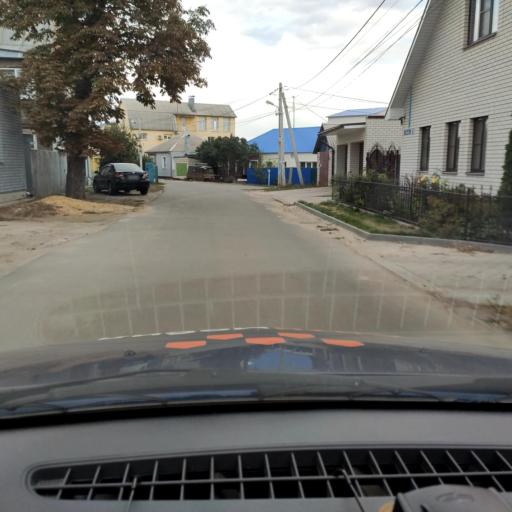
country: RU
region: Voronezj
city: Voronezh
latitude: 51.6279
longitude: 39.1969
